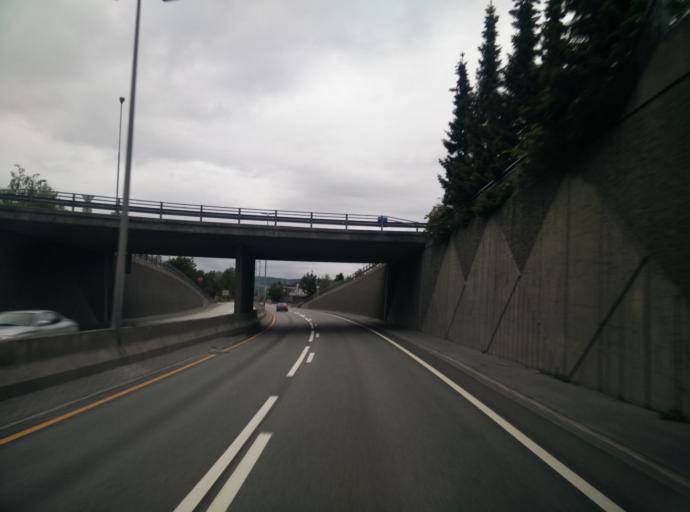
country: NO
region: Sor-Trondelag
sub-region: Trondheim
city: Trondheim
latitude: 63.4078
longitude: 10.4213
